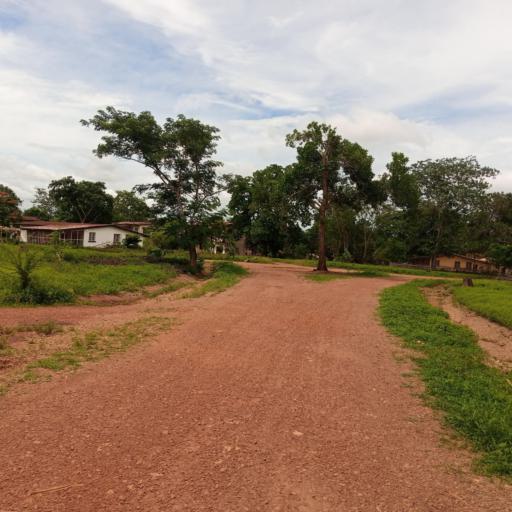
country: SL
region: Southern Province
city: Largo
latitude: 8.1122
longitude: -12.0764
